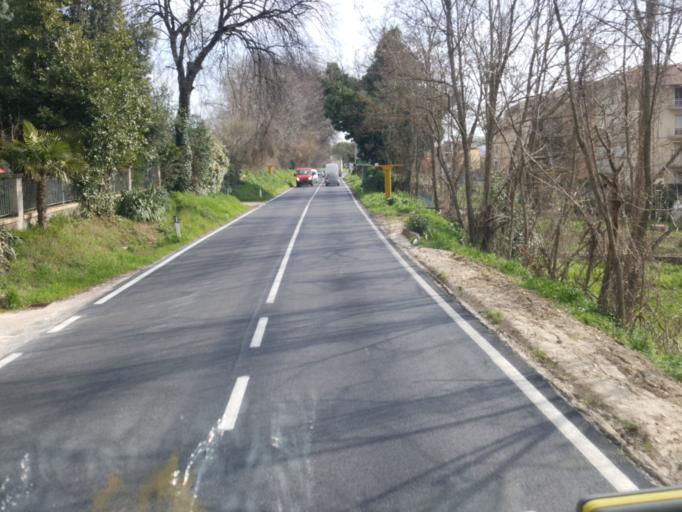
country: IT
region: The Marches
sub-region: Provincia di Macerata
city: Passo di Treia
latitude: 43.2799
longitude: 13.3176
